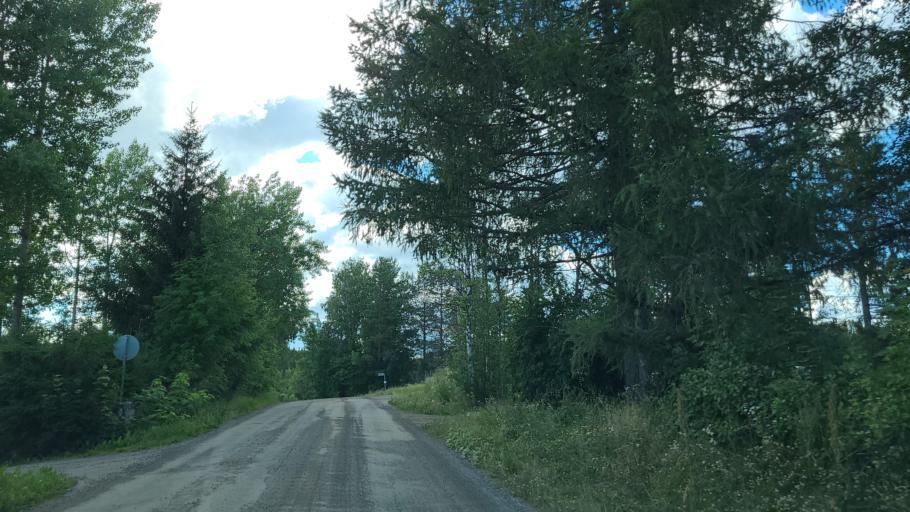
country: FI
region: Central Finland
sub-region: Jaemsae
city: Jaemsae
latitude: 61.9346
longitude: 25.3378
